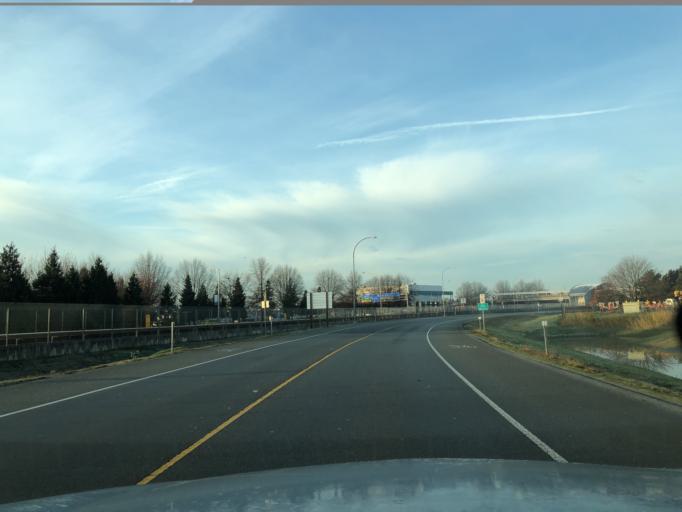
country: CA
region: British Columbia
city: Richmond
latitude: 49.1939
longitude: -123.1534
